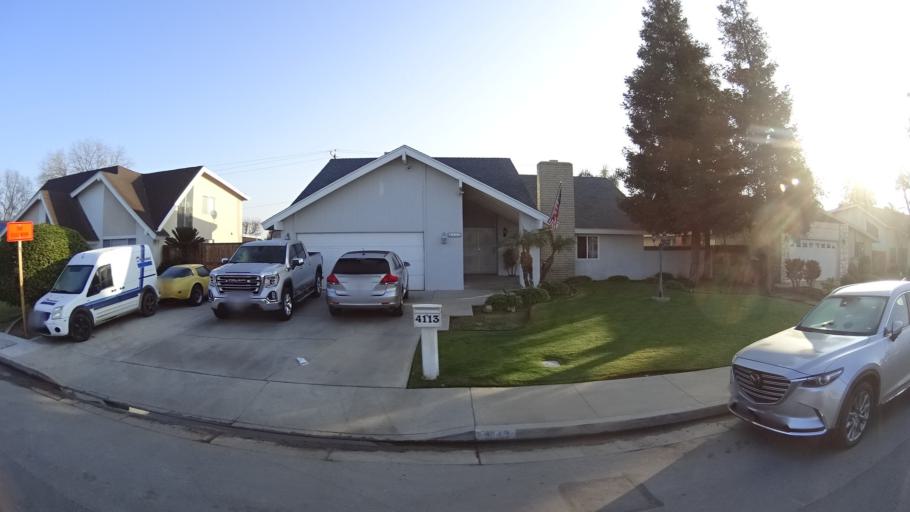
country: US
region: California
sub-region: Kern County
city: Bakersfield
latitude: 35.3597
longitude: -119.0498
